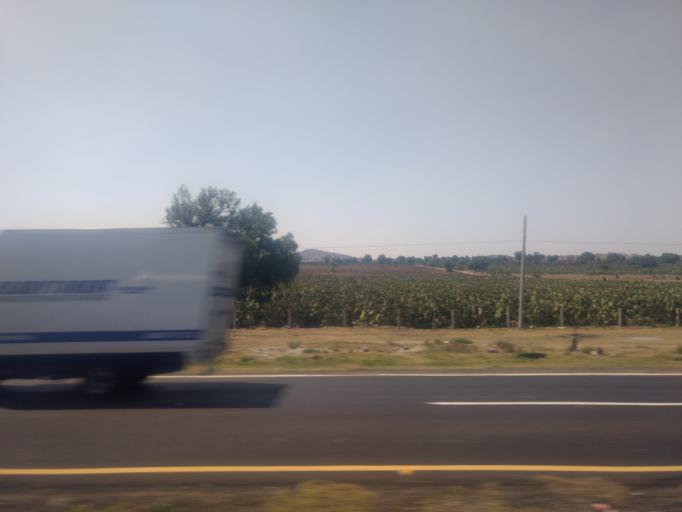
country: MX
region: Morelos
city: Nopaltepec
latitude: 19.7924
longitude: -98.7302
